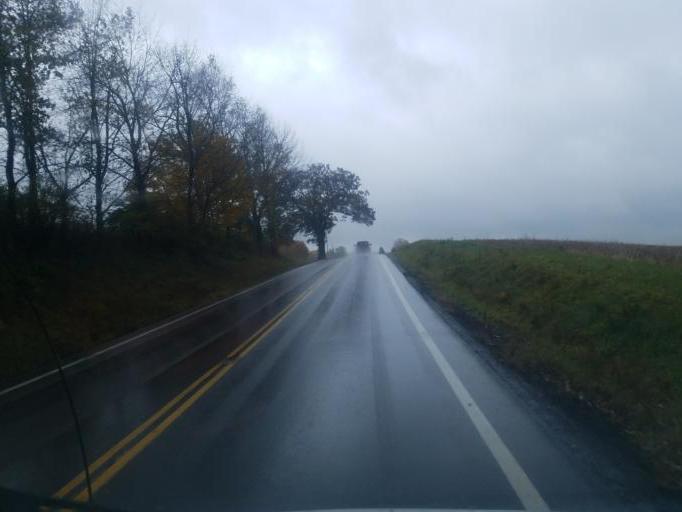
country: US
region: Ohio
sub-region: Knox County
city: Mount Vernon
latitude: 40.3597
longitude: -82.4519
